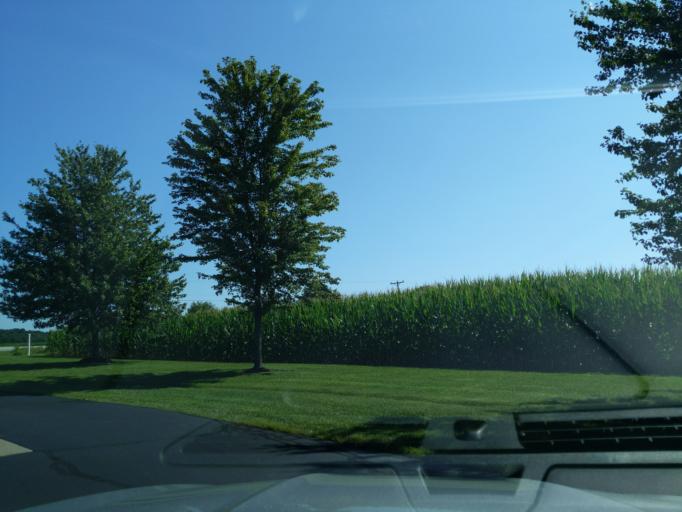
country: US
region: Indiana
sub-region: Ripley County
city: Osgood
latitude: 39.0744
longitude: -85.3750
